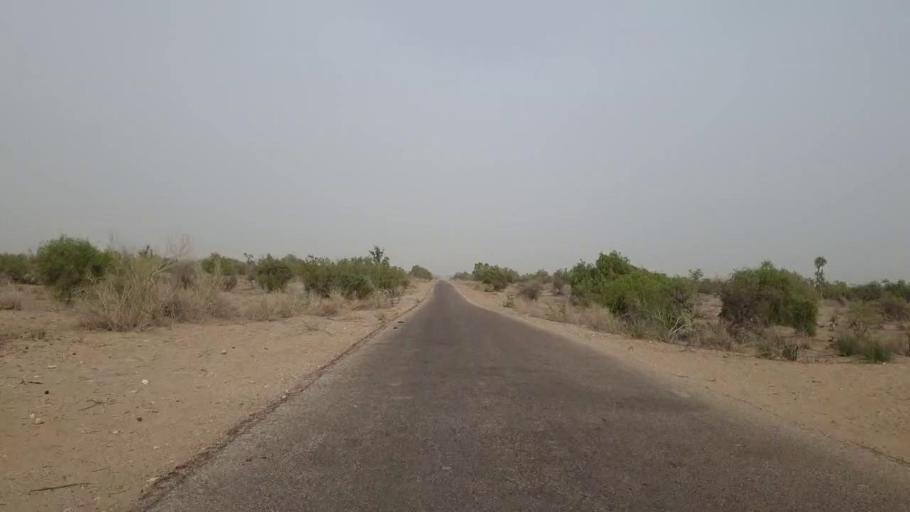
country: PK
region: Sindh
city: Islamkot
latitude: 24.5707
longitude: 70.3218
